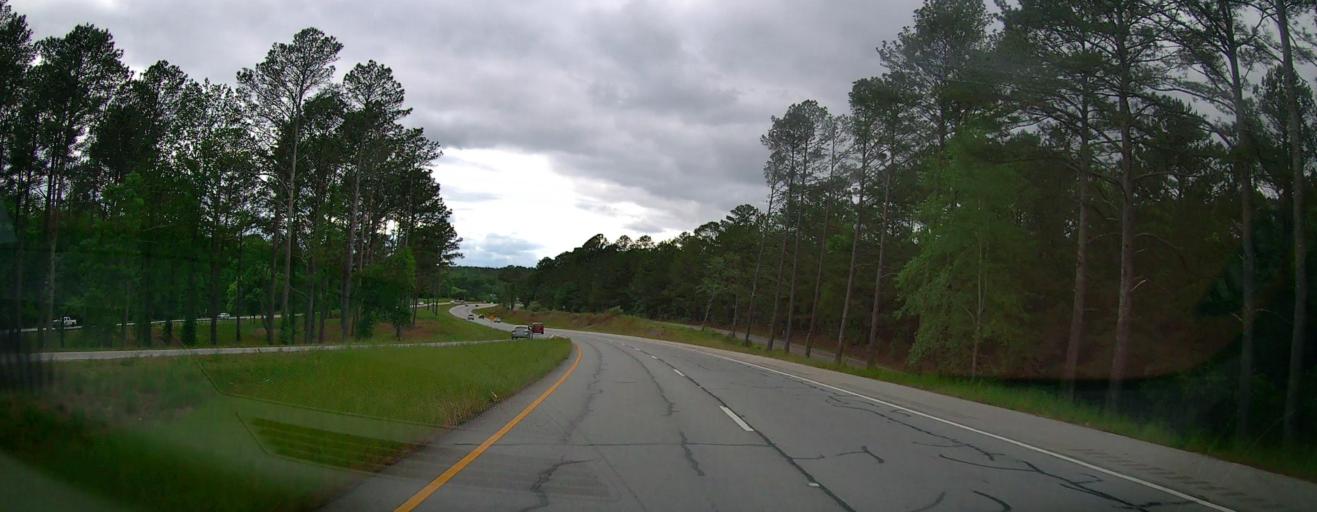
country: US
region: Georgia
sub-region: Walton County
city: Monroe
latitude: 33.8039
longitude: -83.7500
